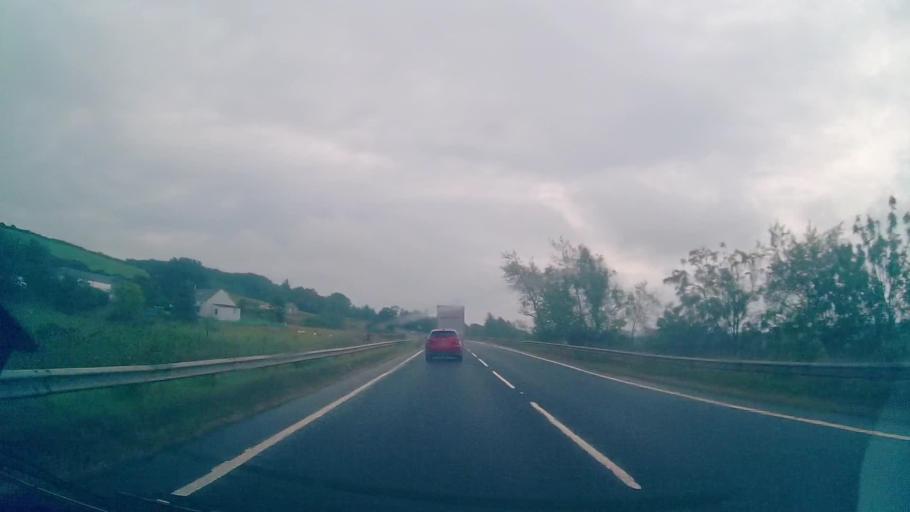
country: GB
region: Scotland
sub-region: Dumfries and Galloway
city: Lochmaben
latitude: 55.0374
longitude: -3.4330
